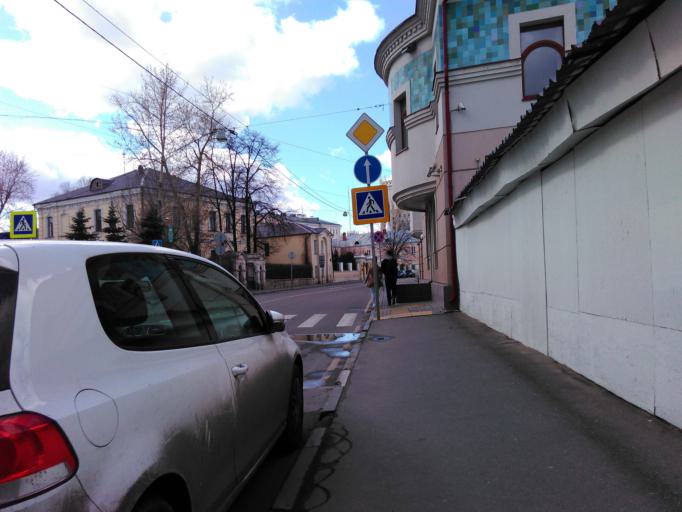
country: RU
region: Moscow
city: Zamoskvorech'ye
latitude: 55.7445
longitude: 37.6481
